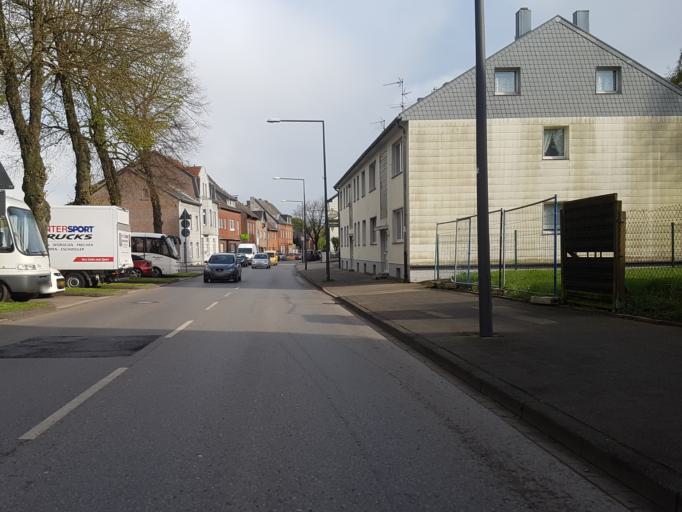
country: DE
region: North Rhine-Westphalia
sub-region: Regierungsbezirk Koln
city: Wurselen
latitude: 50.7817
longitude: 6.1613
